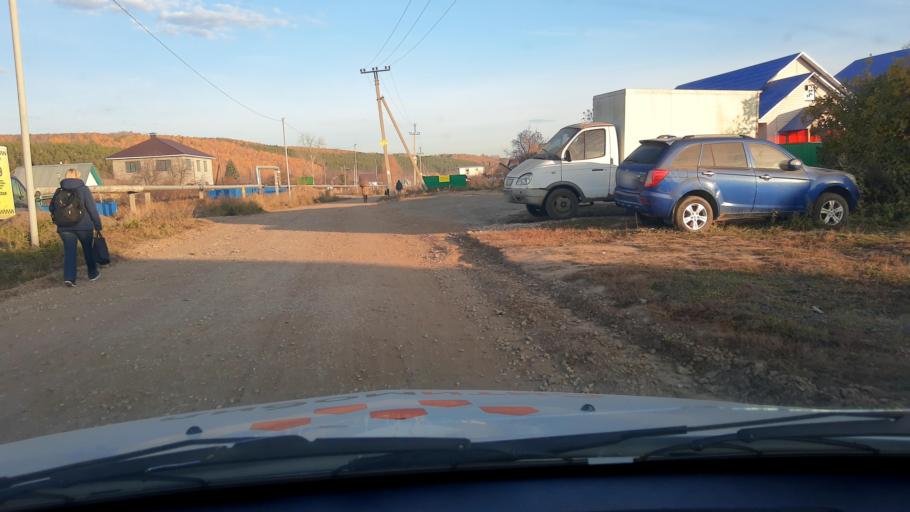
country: RU
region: Bashkortostan
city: Ufa
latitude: 54.8138
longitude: 56.1554
